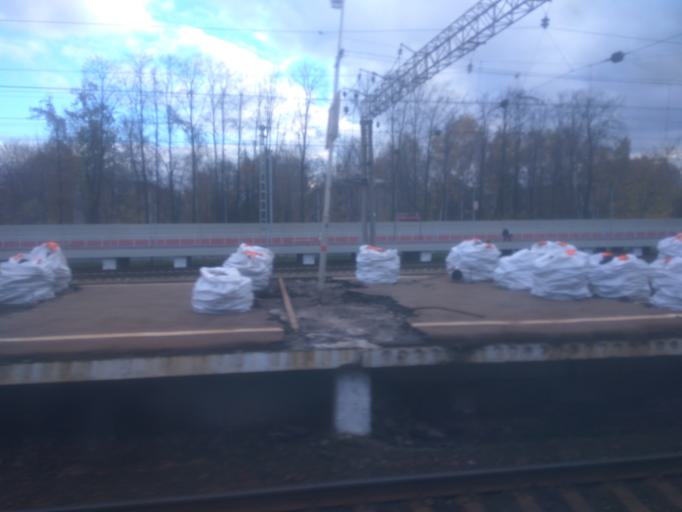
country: RU
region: Moscow
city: Solntsevo
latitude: 55.6580
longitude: 37.3869
